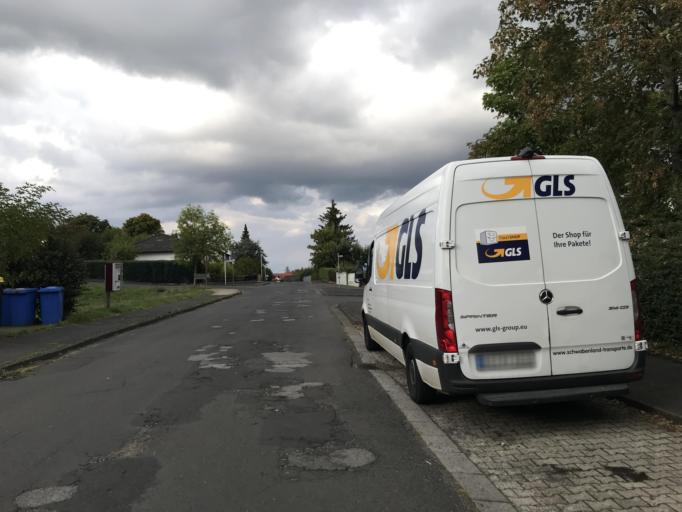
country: DE
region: Hesse
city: Borken
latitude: 51.0384
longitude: 9.2890
